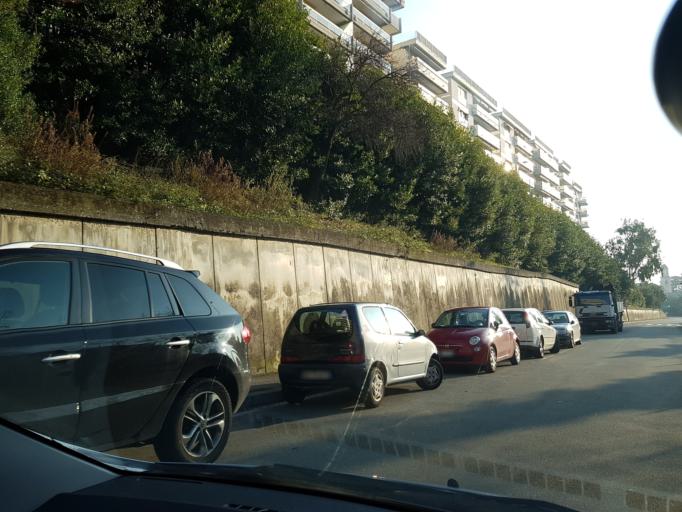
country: IT
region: Liguria
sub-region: Provincia di Genova
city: Bogliasco
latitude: 44.3972
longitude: 9.0062
